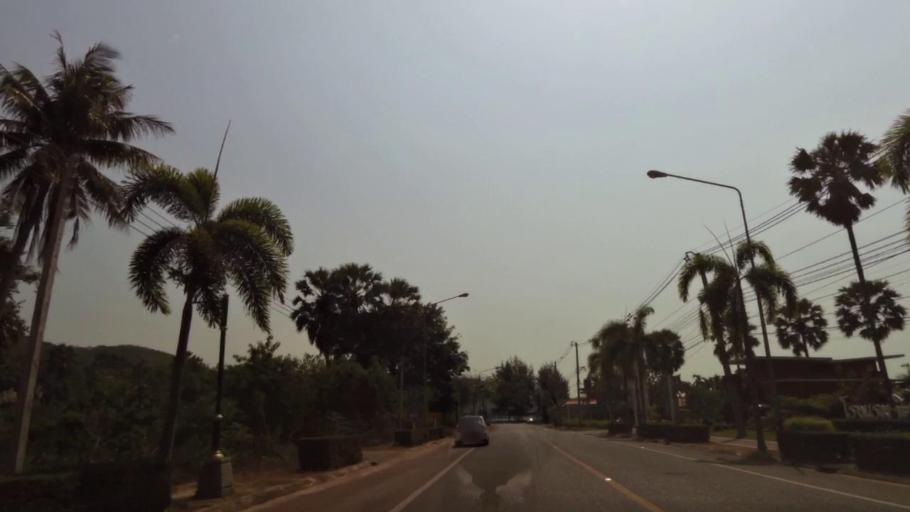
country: TH
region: Chanthaburi
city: Tha Mai
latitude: 12.5344
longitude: 101.9418
